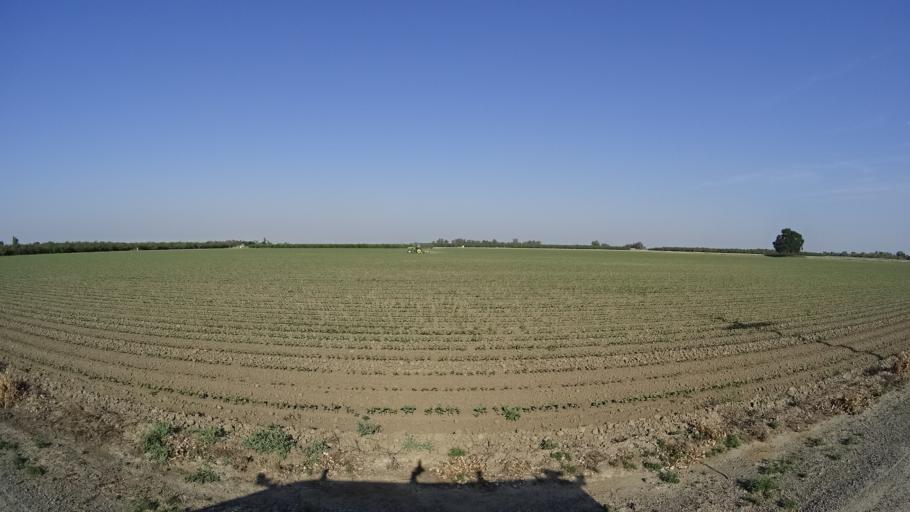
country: US
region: California
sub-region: Fresno County
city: Riverdale
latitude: 36.3729
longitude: -119.8603
